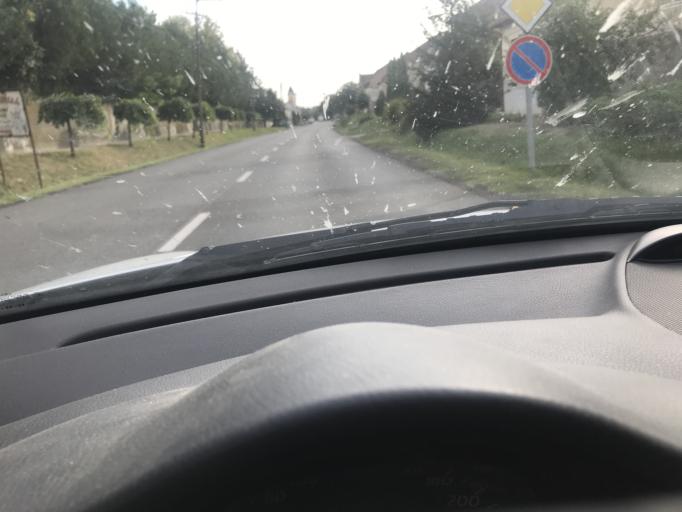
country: HU
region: Bacs-Kiskun
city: Csaszartoltes
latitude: 46.4269
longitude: 19.1810
